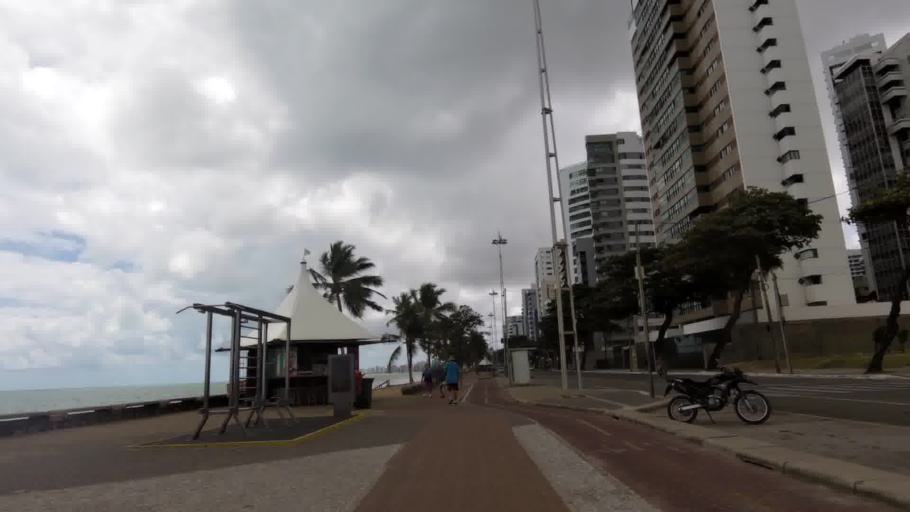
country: BR
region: Pernambuco
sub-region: Recife
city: Recife
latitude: -8.1423
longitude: -34.9037
